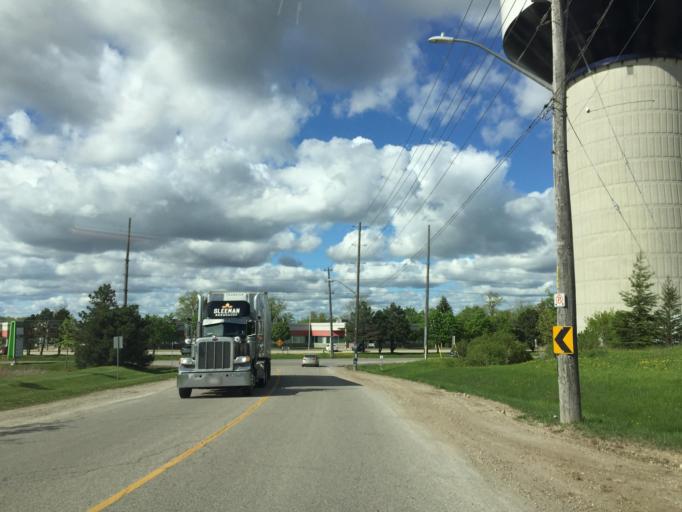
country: CA
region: Ontario
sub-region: Wellington County
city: Guelph
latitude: 43.4920
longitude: -80.2003
